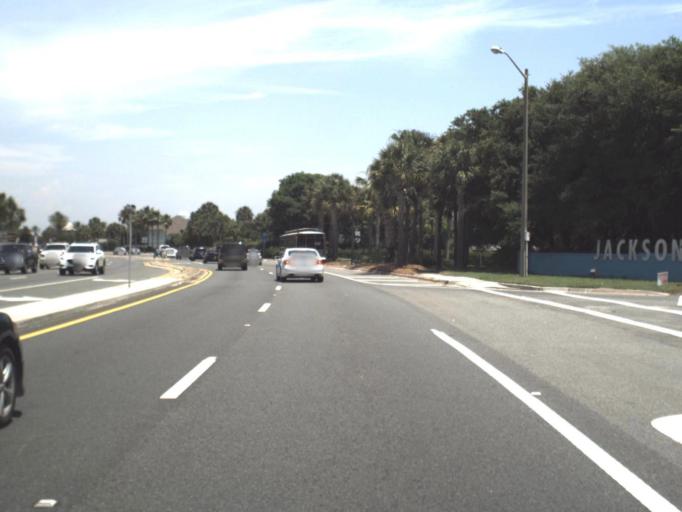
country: US
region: Florida
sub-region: Saint Johns County
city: Ponte Vedra Beach
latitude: 30.2607
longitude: -81.3870
